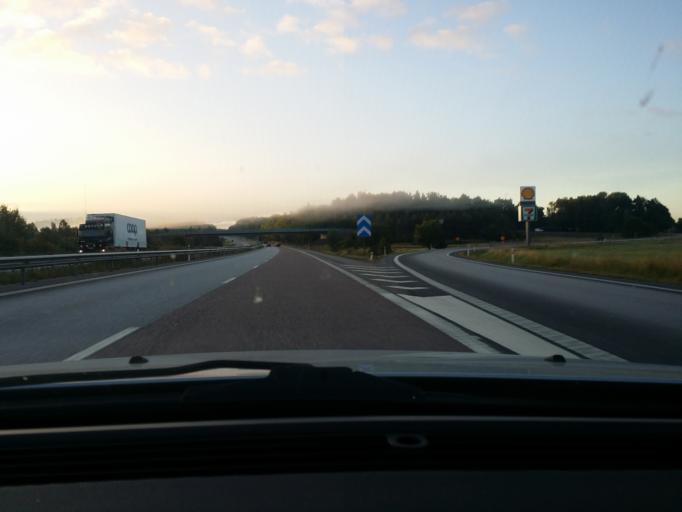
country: SE
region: Uppsala
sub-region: Habo Kommun
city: Balsta
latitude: 59.5875
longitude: 17.5037
